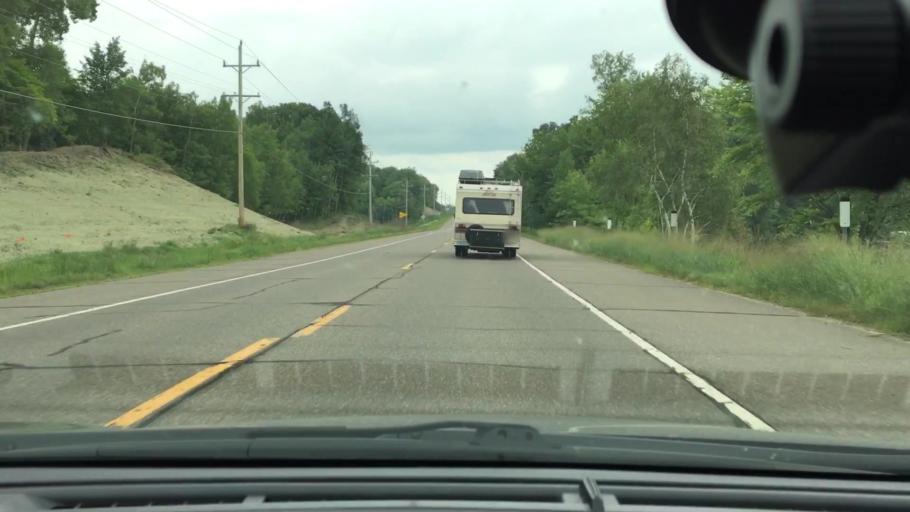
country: US
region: Minnesota
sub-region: Crow Wing County
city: Crosby
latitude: 46.4887
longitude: -93.9080
